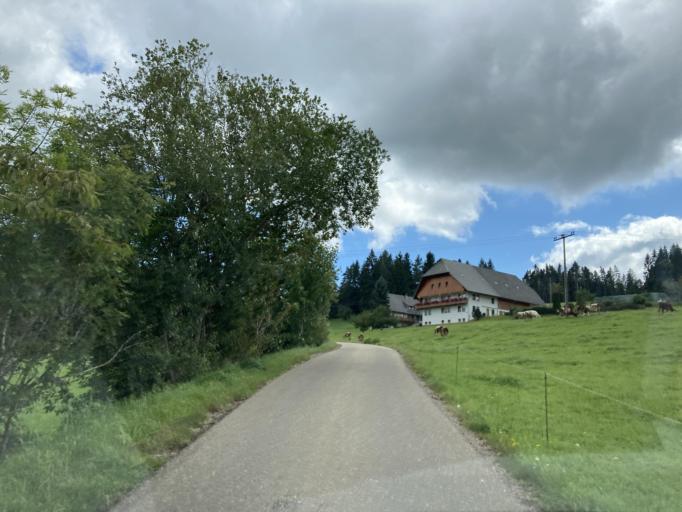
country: DE
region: Baden-Wuerttemberg
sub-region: Freiburg Region
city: Sankt Georgen im Schwarzwald
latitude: 48.1060
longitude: 8.3379
